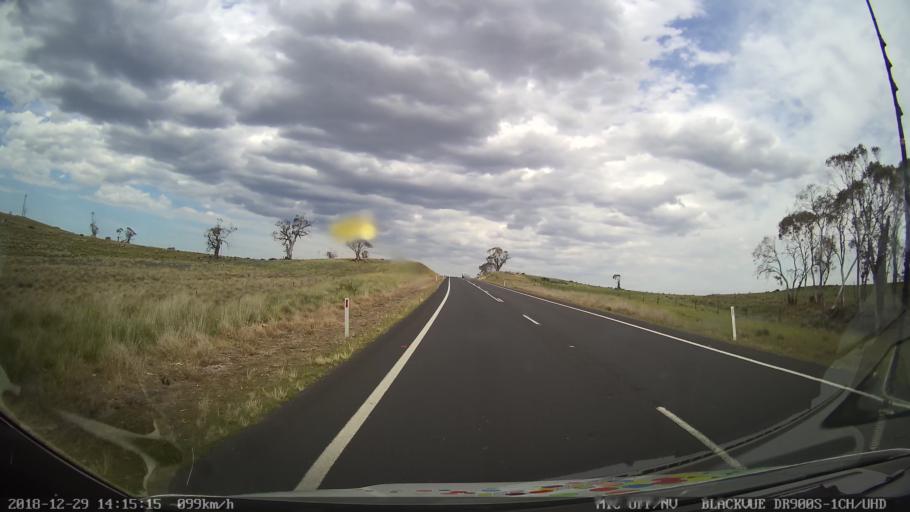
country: AU
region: New South Wales
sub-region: Cooma-Monaro
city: Cooma
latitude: -36.4537
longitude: 149.2391
